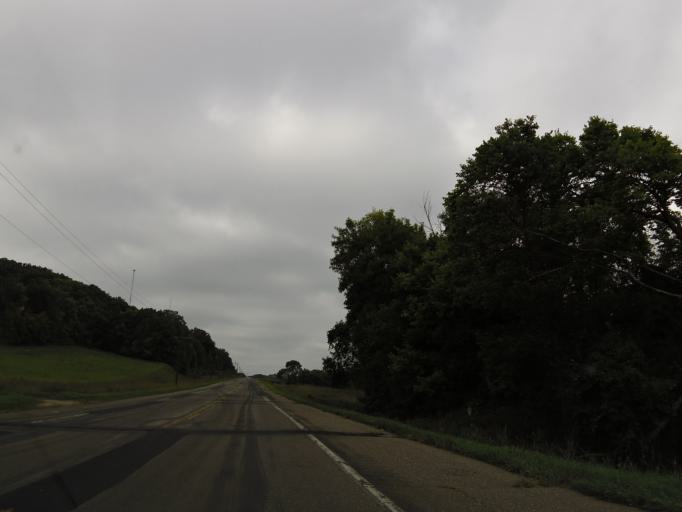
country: US
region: Minnesota
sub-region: Yellow Medicine County
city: Granite Falls
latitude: 44.8528
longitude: -95.6215
